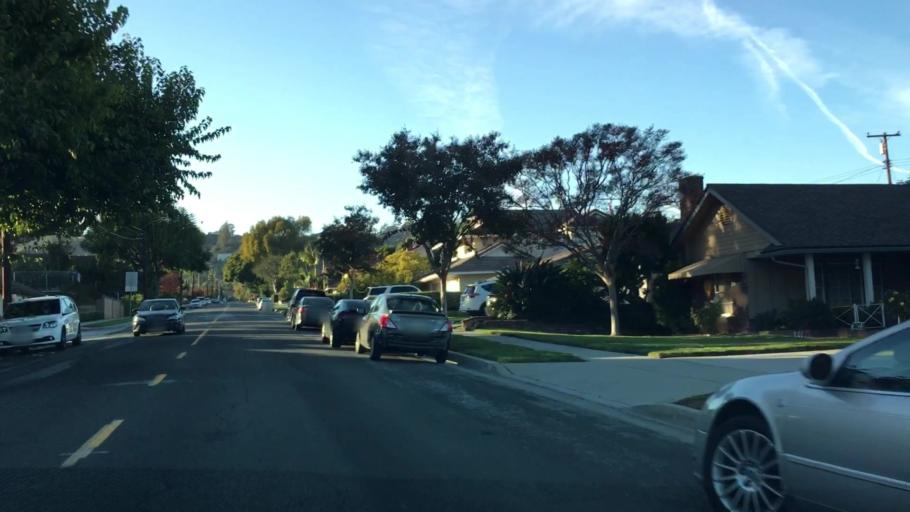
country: US
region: California
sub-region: Los Angeles County
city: Hacienda Heights
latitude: 33.9891
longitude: -117.9808
